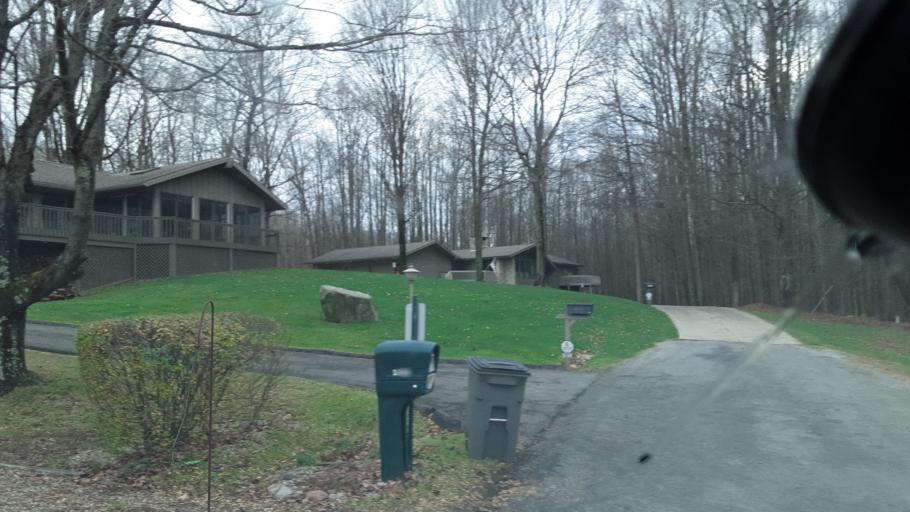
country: US
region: Ohio
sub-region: Richland County
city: Lexington
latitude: 40.6954
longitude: -82.6170
